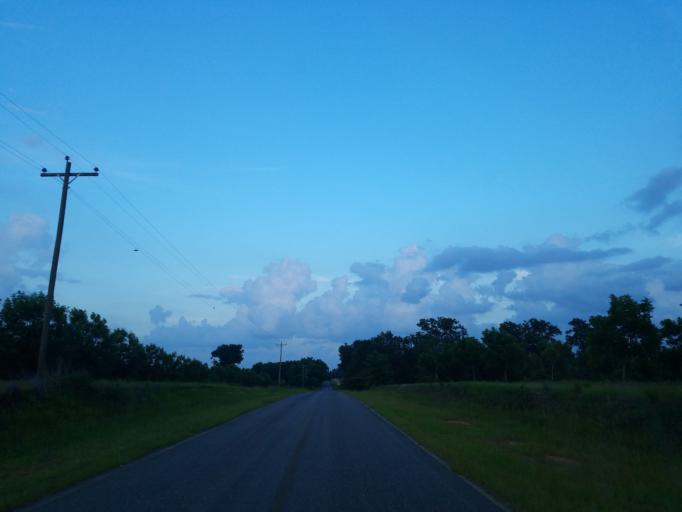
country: US
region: Georgia
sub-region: Dooly County
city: Unadilla
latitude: 32.1715
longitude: -83.7392
